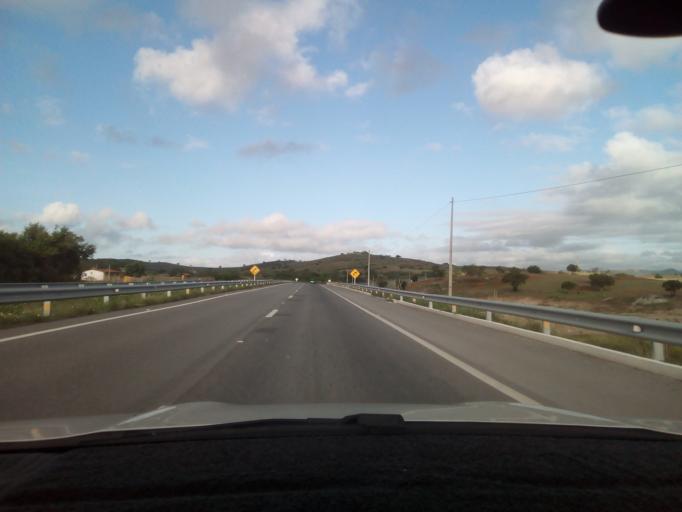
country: BR
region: Paraiba
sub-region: Mogeiro
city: Mogeiro
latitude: -7.2080
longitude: -35.5277
